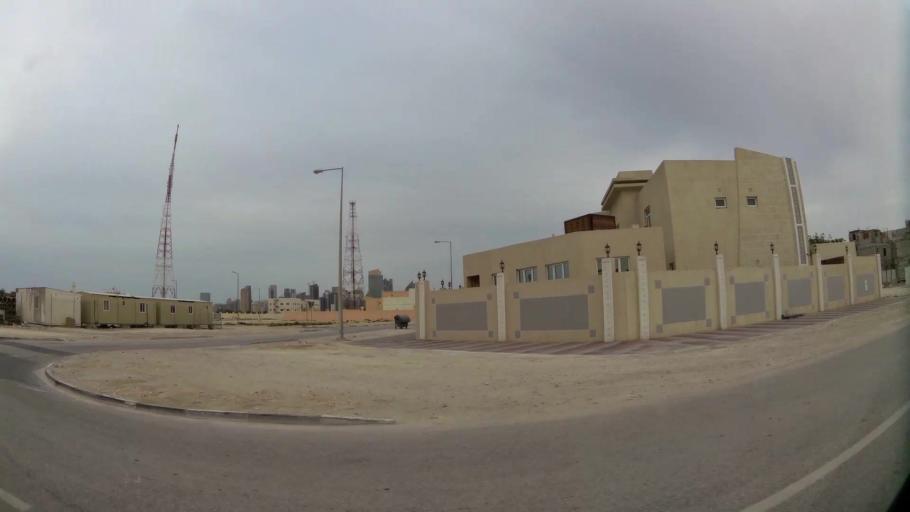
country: QA
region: Baladiyat ad Dawhah
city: Doha
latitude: 25.3097
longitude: 51.5008
